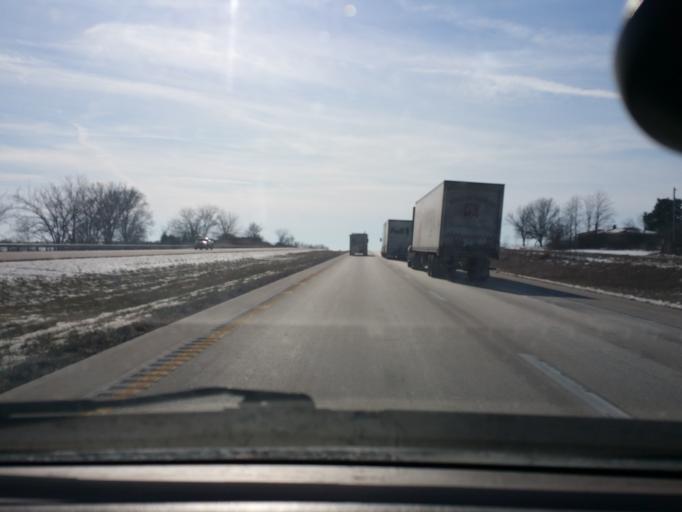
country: US
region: Missouri
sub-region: Clinton County
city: Cameron
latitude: 39.6506
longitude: -94.2403
